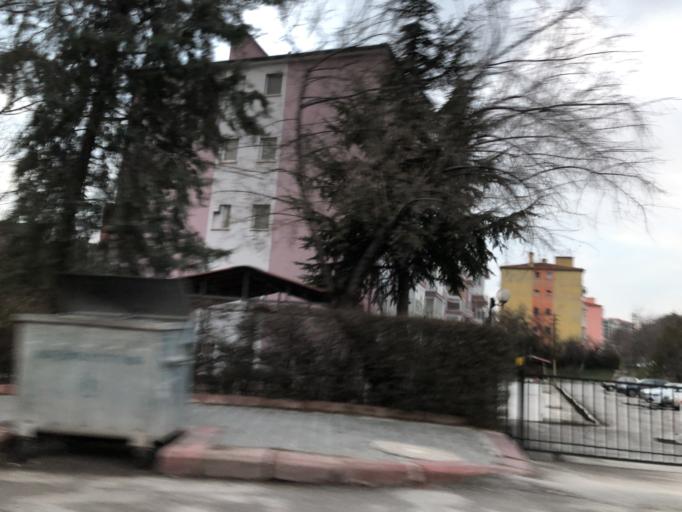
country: TR
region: Ankara
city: Ankara
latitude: 39.9607
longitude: 32.8110
